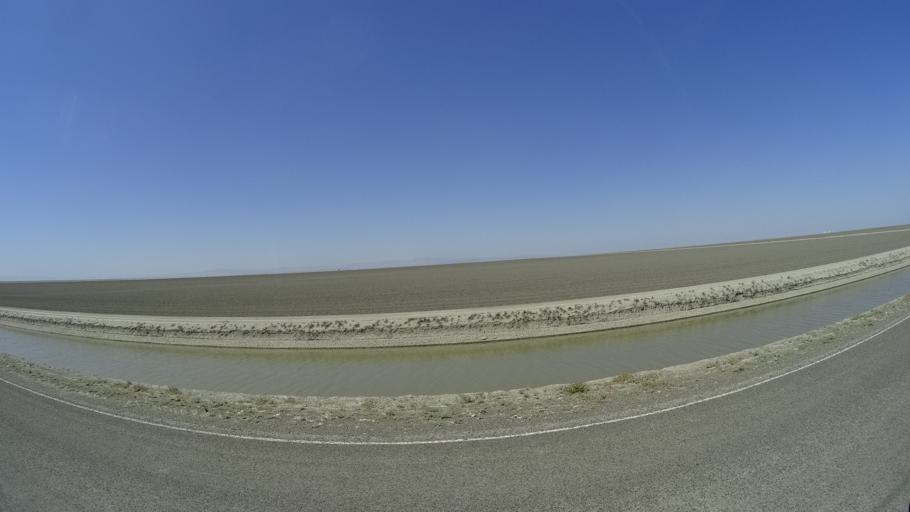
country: US
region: California
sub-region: Kings County
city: Corcoran
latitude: 35.9684
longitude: -119.6432
